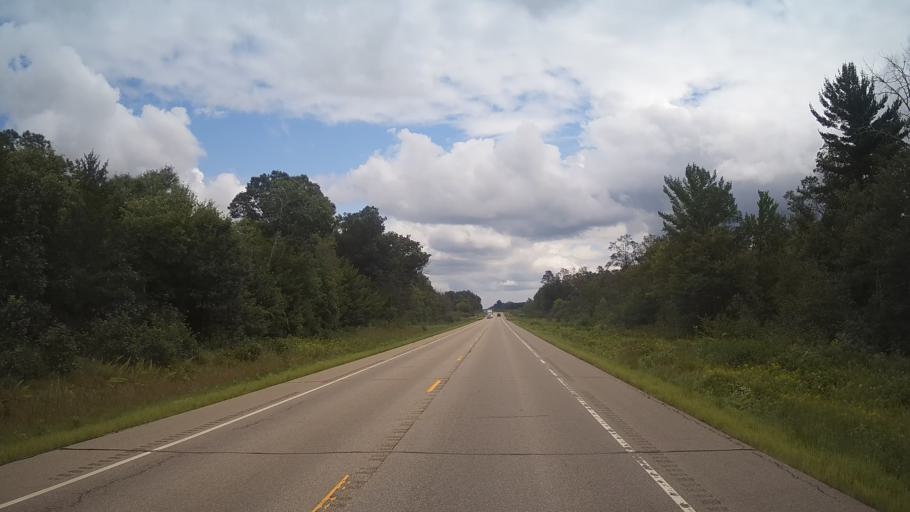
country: US
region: Wisconsin
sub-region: Adams County
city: Friendship
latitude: 44.0251
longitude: -89.7675
